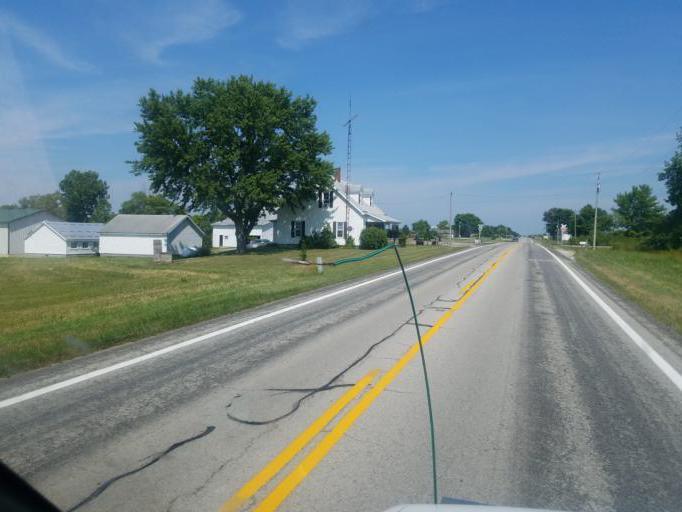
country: US
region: Ohio
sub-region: Auglaize County
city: Saint Marys
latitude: 40.4951
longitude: -84.3930
